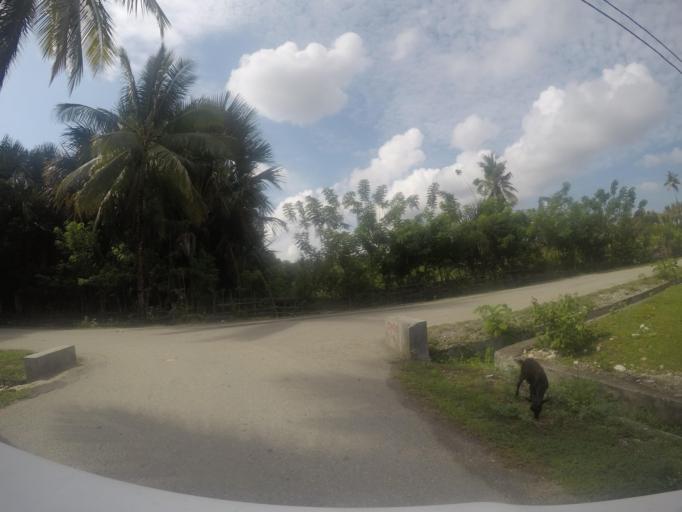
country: TL
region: Viqueque
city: Viqueque
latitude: -8.8532
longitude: 126.3580
